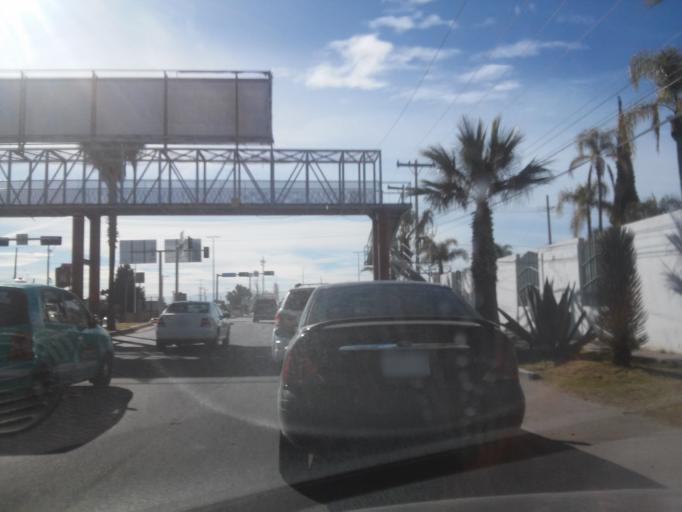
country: MX
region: Durango
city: Victoria de Durango
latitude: 24.0401
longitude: -104.6581
